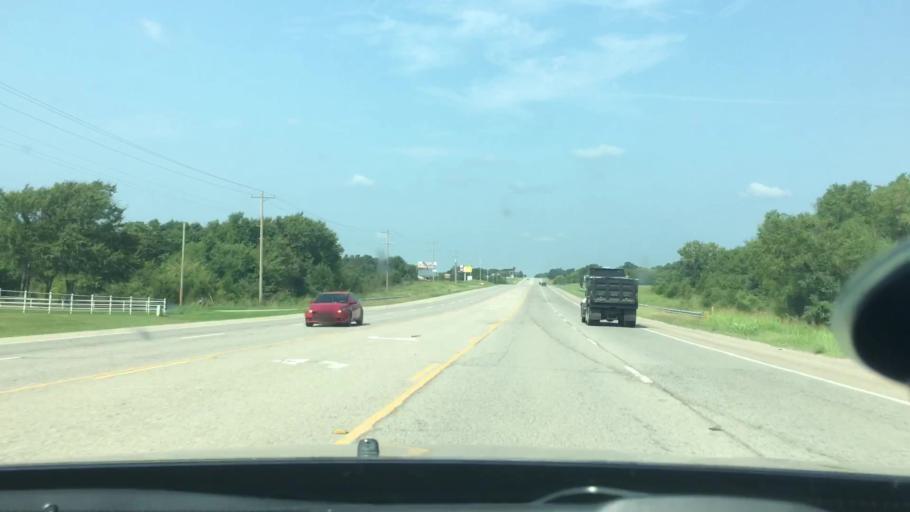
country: US
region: Oklahoma
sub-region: Bryan County
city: Calera
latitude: 33.9982
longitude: -96.4755
